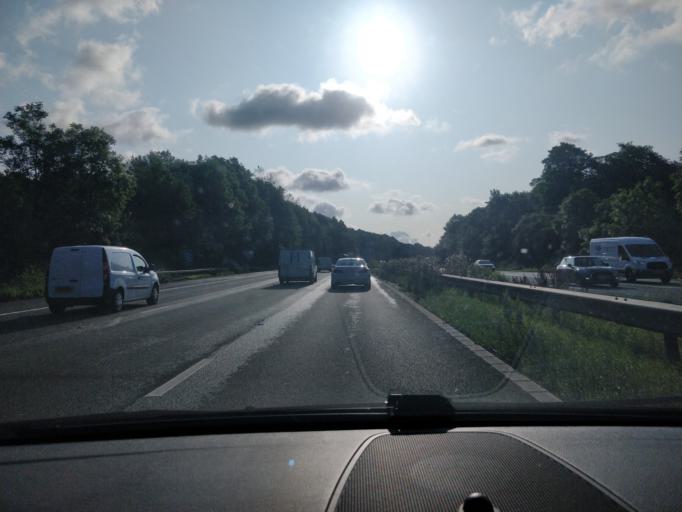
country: GB
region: England
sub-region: Knowsley
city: Huyton
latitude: 53.4302
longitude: -2.8332
